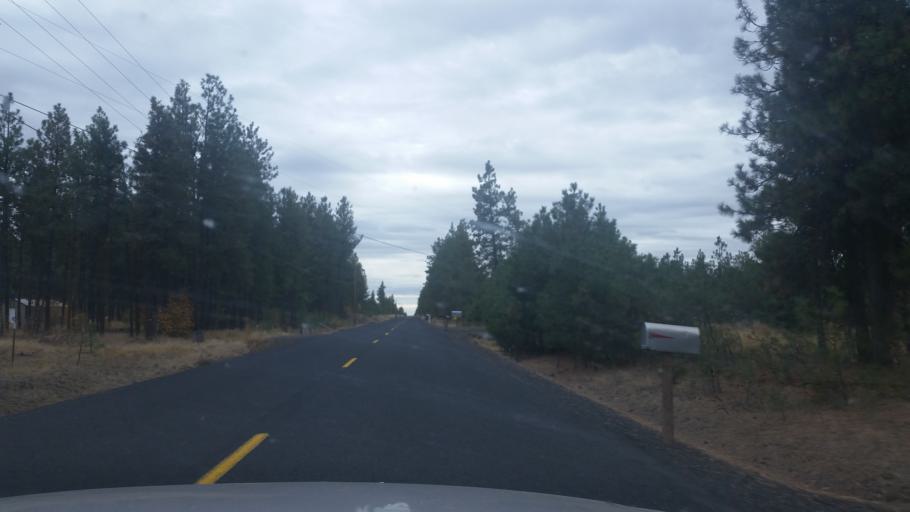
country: US
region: Washington
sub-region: Spokane County
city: Medical Lake
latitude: 47.4729
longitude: -117.7792
